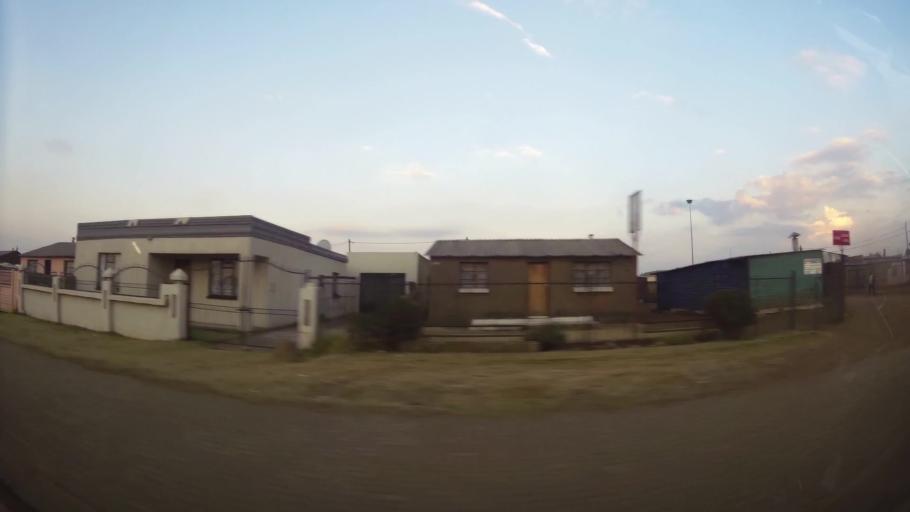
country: ZA
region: Gauteng
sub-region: City of Johannesburg Metropolitan Municipality
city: Orange Farm
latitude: -26.5515
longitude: 27.8640
